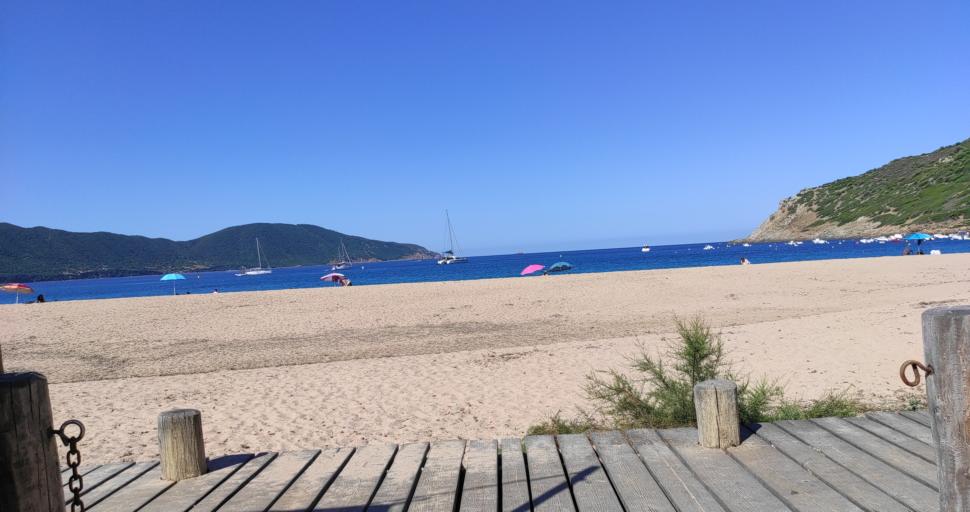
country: FR
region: Corsica
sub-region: Departement de la Corse-du-Sud
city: Alata
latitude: 41.9921
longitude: 8.6693
